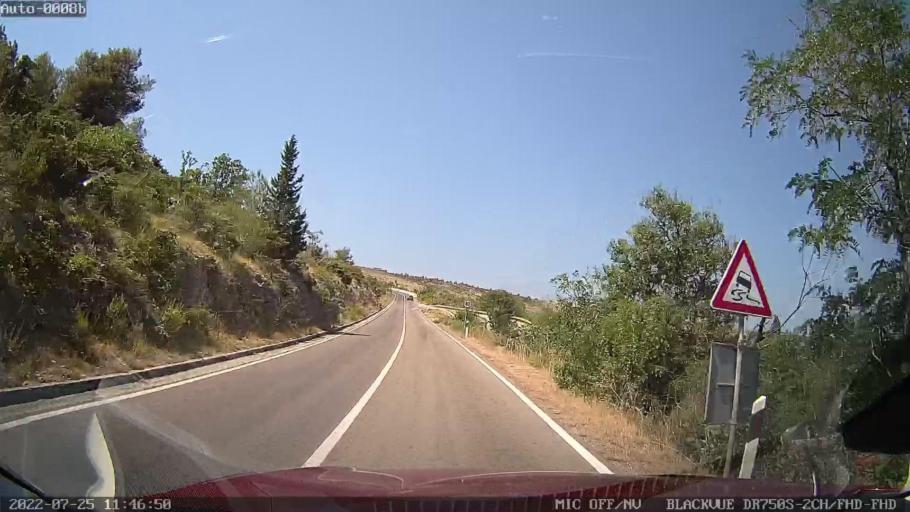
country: HR
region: Zadarska
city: Razanac
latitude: 44.2418
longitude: 15.3021
